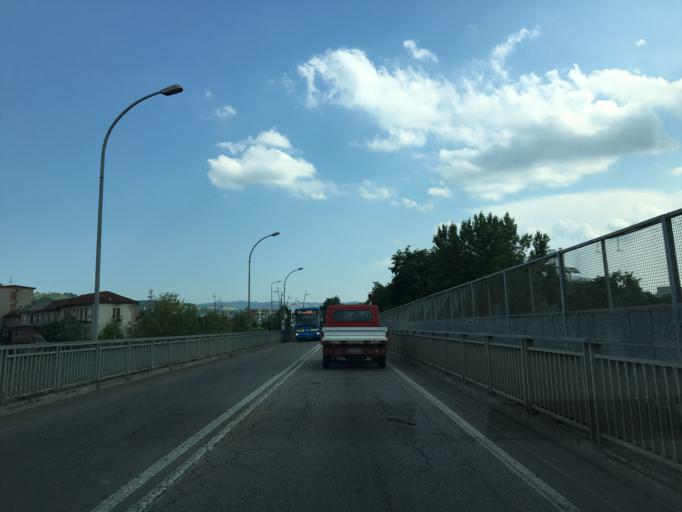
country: IT
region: Piedmont
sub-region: Provincia di Cuneo
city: Alba
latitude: 44.7056
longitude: 8.0274
